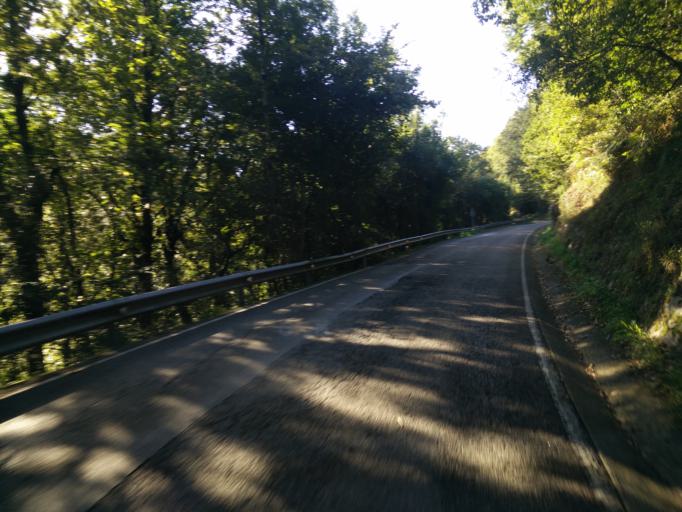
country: ES
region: Cantabria
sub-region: Provincia de Cantabria
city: San Pedro del Romeral
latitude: 43.1383
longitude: -3.8153
